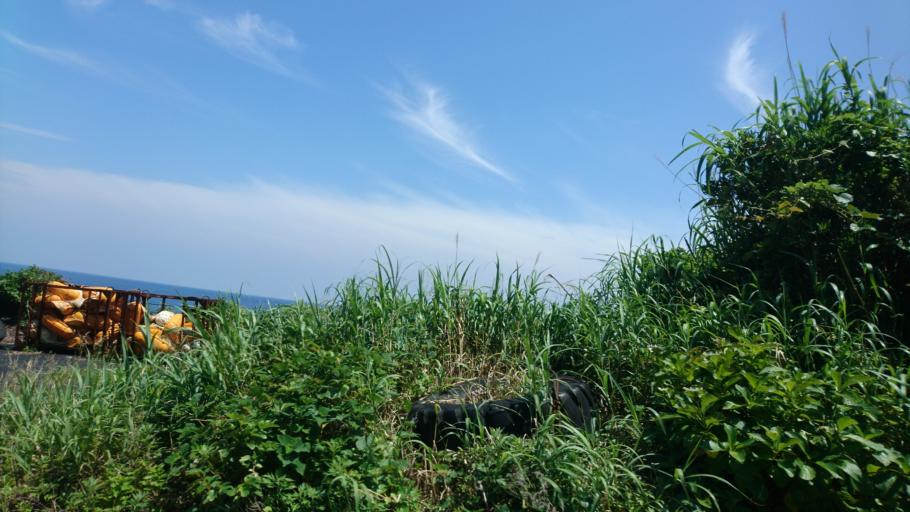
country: JP
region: Shizuoka
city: Shimoda
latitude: 34.3941
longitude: 139.2792
